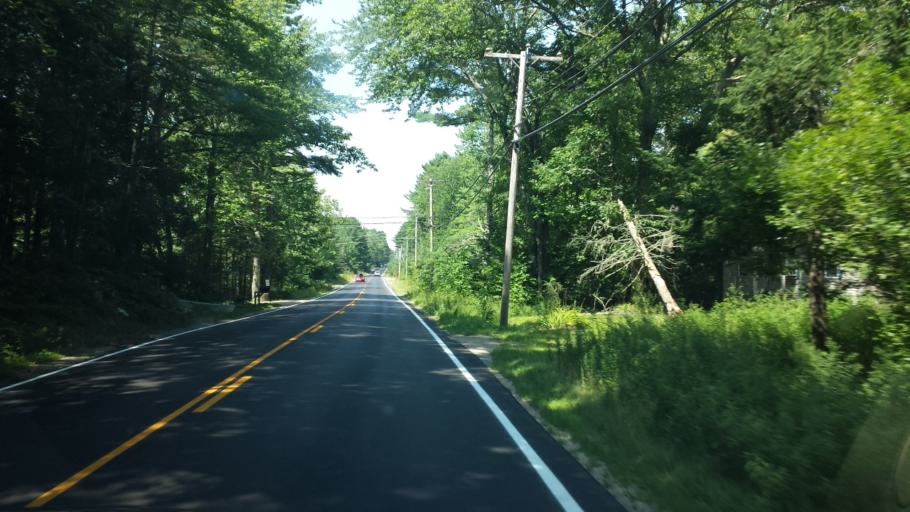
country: US
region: Maine
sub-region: York County
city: Arundel
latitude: 43.3987
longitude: -70.4855
